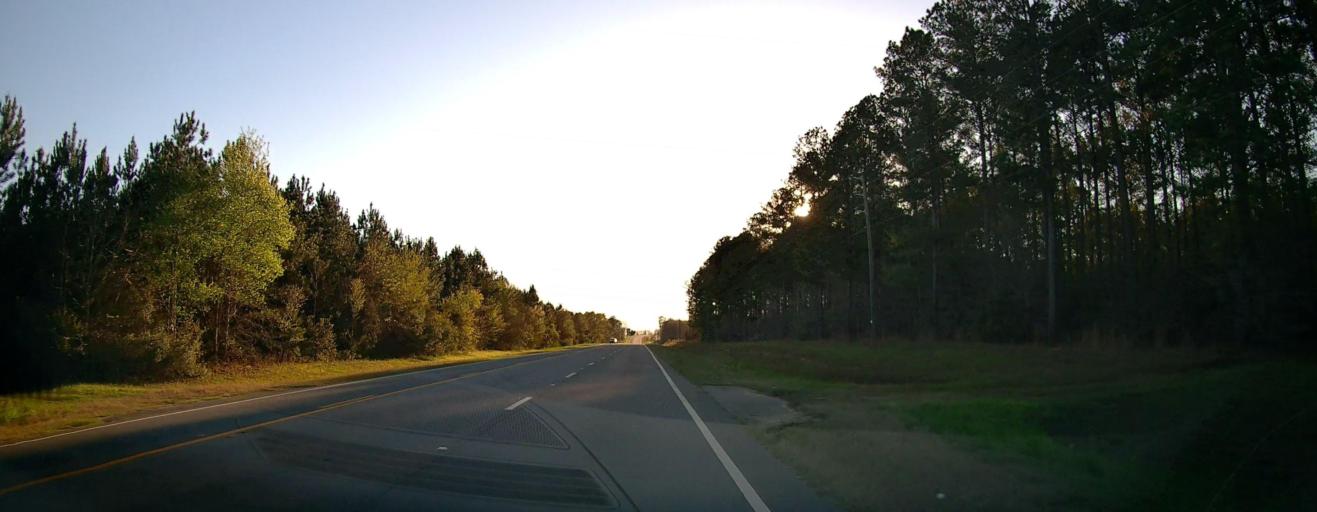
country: US
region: Georgia
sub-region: Wilcox County
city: Rochelle
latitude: 31.9643
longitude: -83.3918
